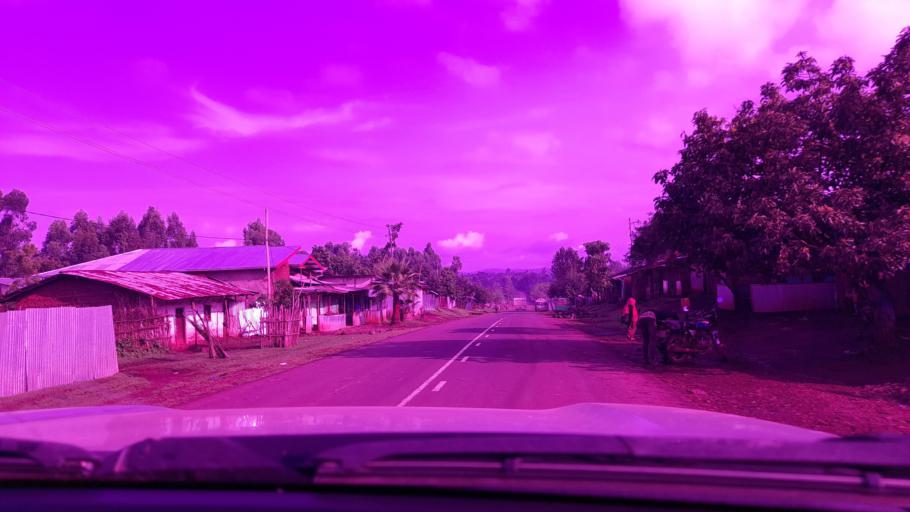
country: ET
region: Oromiya
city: Bedele
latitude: 8.1759
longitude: 36.4582
